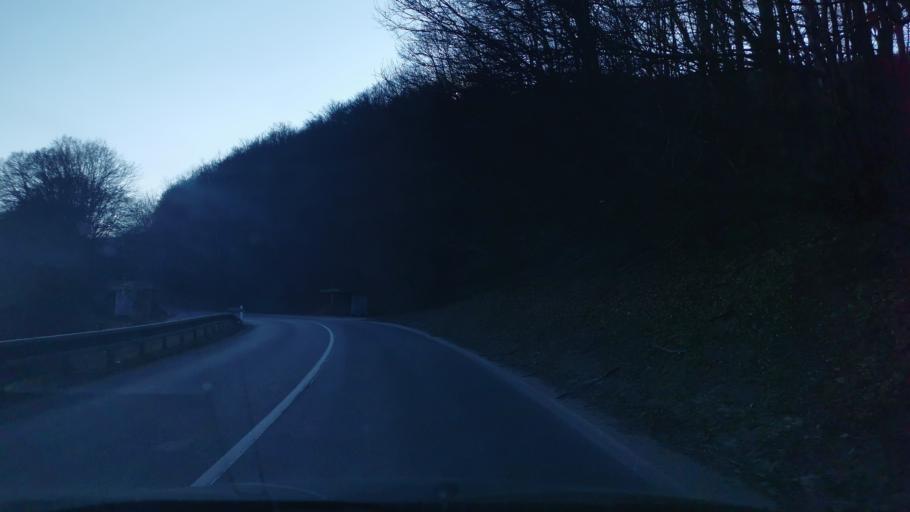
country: SK
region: Trenciansky
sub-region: Okres Myjava
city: Myjava
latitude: 48.7504
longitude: 17.4884
